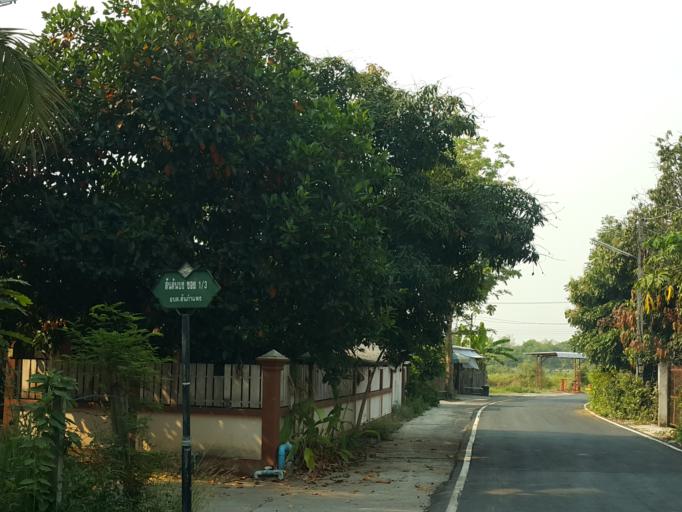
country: TH
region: Chiang Mai
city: San Kamphaeng
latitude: 18.7444
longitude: 99.0945
